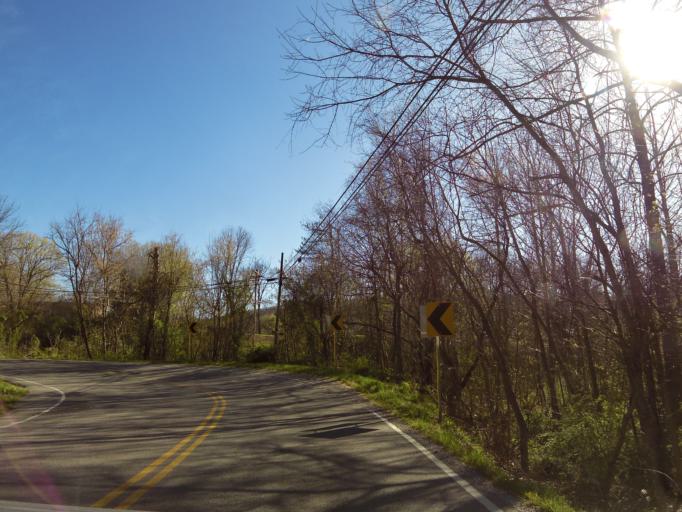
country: US
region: Tennessee
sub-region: Scott County
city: Huntsville
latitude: 36.3380
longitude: -84.3865
